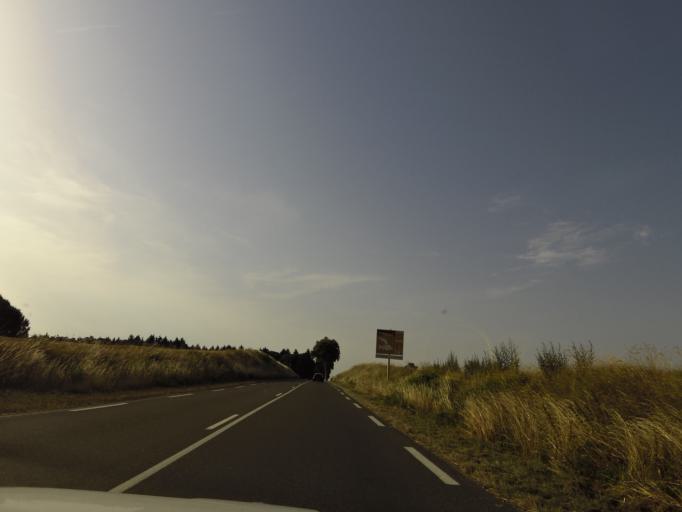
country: FR
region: Rhone-Alpes
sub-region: Departement de l'Ain
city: Meximieux
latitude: 45.9257
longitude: 5.1870
